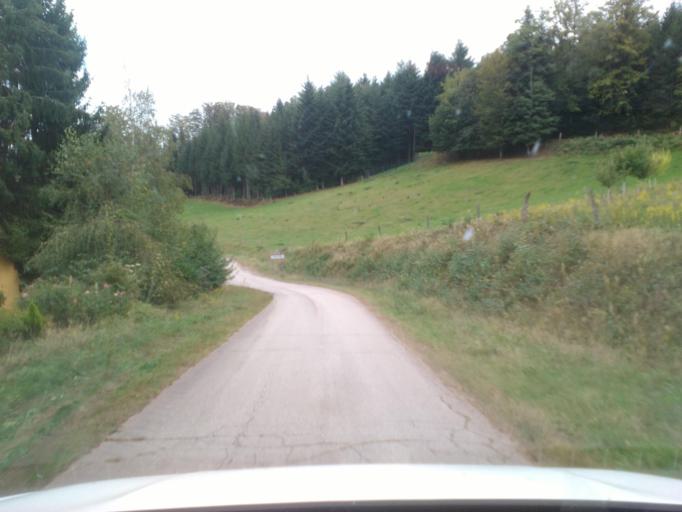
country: FR
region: Lorraine
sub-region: Departement des Vosges
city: Senones
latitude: 48.3807
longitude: 7.0153
